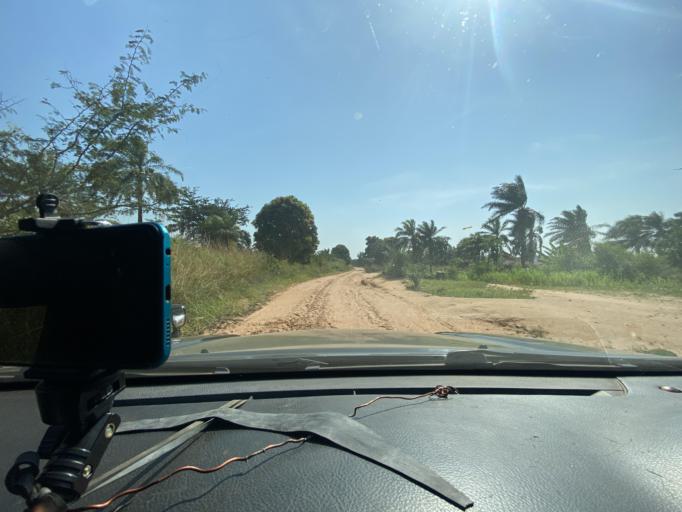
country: CD
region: Kasai-Oriental
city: Kabinda
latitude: -6.1047
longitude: 24.5370
